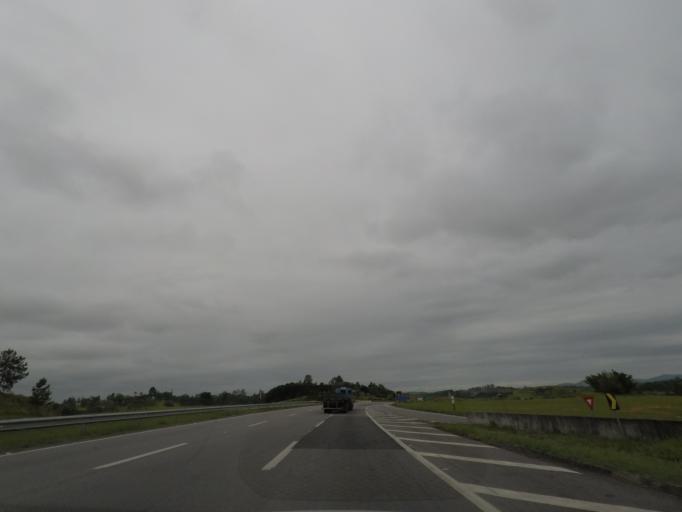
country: BR
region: Sao Paulo
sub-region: Jacarei
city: Jacarei
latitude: -23.3040
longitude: -46.0448
